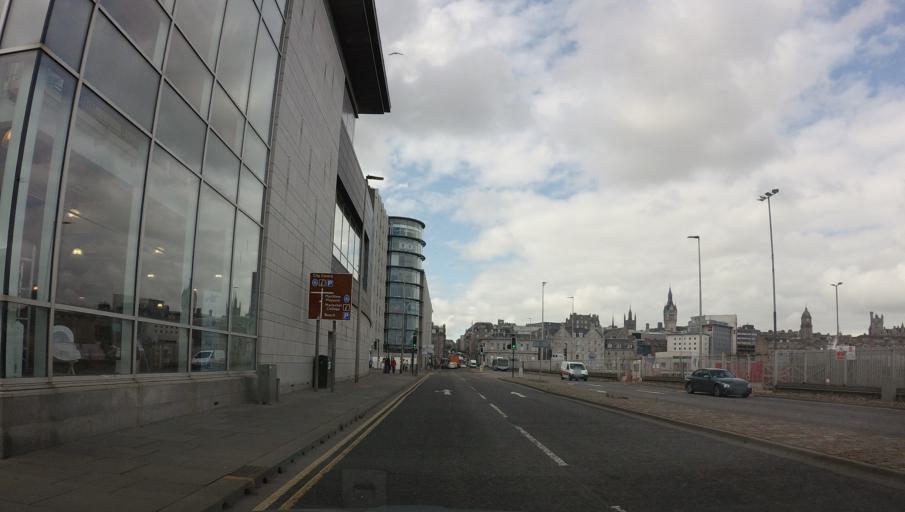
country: GB
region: Scotland
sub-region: Aberdeen City
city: Aberdeen
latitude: 57.1437
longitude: -2.0940
